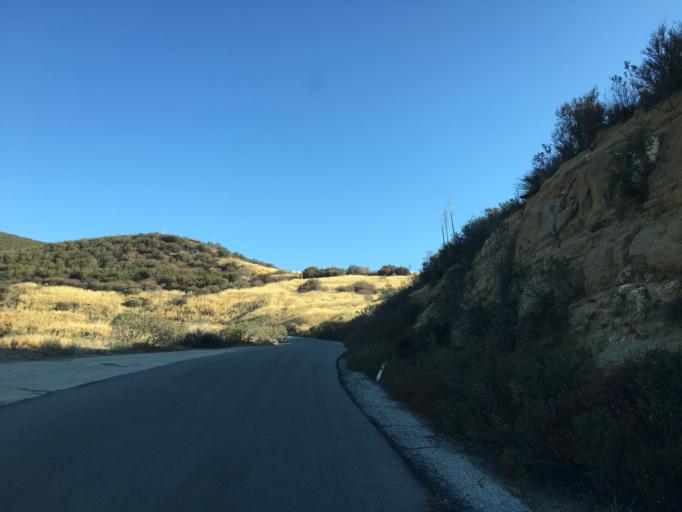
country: US
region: California
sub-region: Los Angeles County
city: Castaic
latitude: 34.5872
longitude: -118.6808
